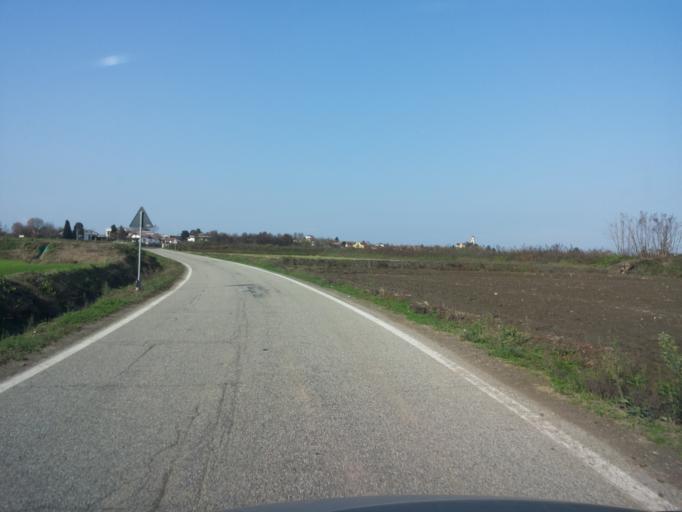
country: IT
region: Piedmont
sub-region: Provincia di Vercelli
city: Pezzana
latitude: 45.2534
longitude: 8.4865
